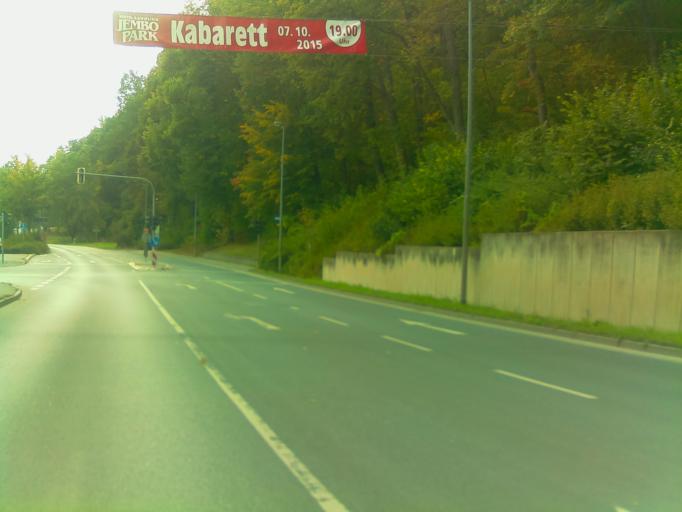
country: DE
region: Thuringia
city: Sulza
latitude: 50.8855
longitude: 11.5882
